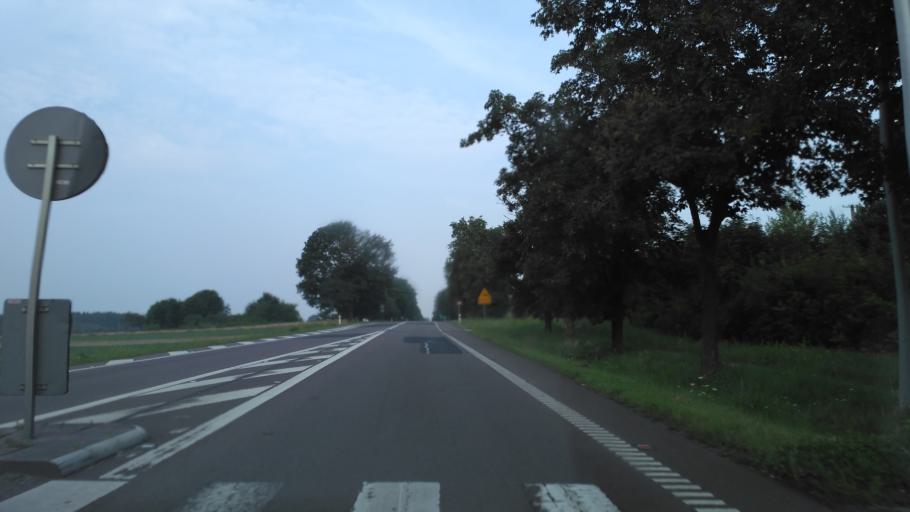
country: PL
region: Lublin Voivodeship
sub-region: Powiat chelmski
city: Rejowiec Fabryczny
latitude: 51.1758
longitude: 23.1753
